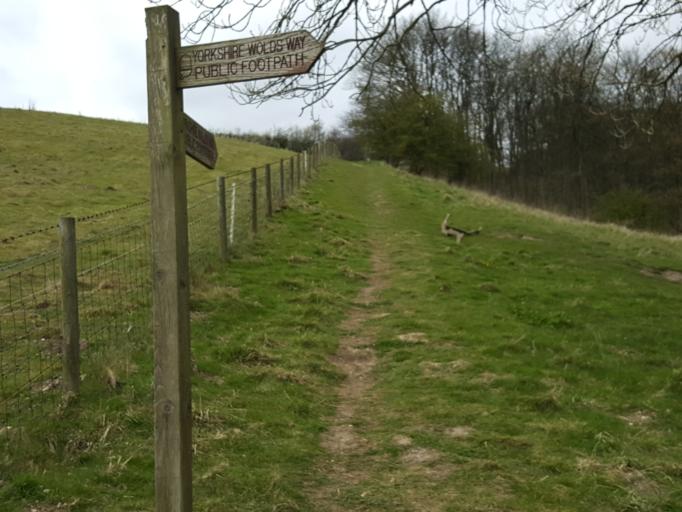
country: GB
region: England
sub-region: East Riding of Yorkshire
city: Brantingham
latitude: 53.7648
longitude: -0.5799
